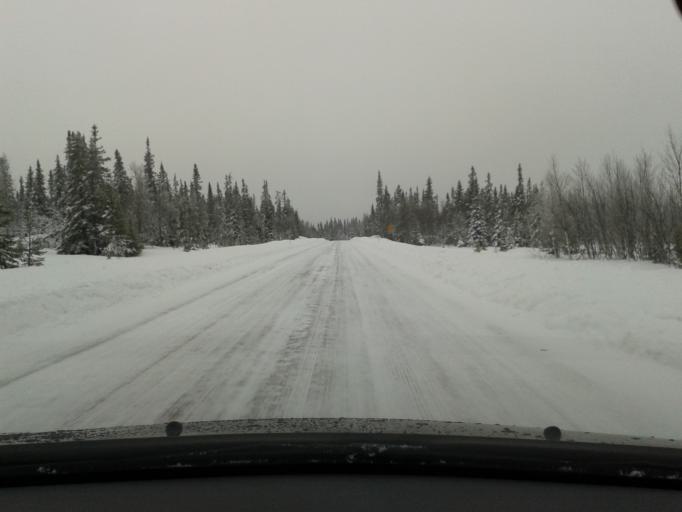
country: SE
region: Vaesterbotten
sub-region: Vilhelmina Kommun
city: Sjoberg
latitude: 65.0919
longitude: 15.8707
